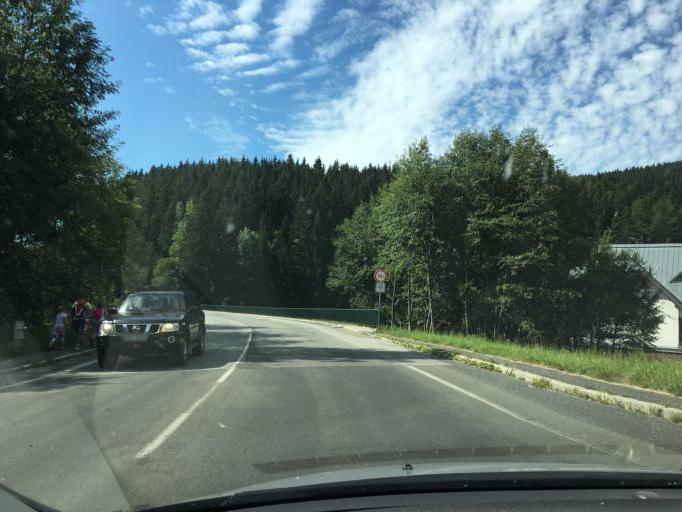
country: CZ
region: Kralovehradecky
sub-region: Okres Trutnov
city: Spindleruv Mlyn
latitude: 50.7150
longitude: 15.5831
